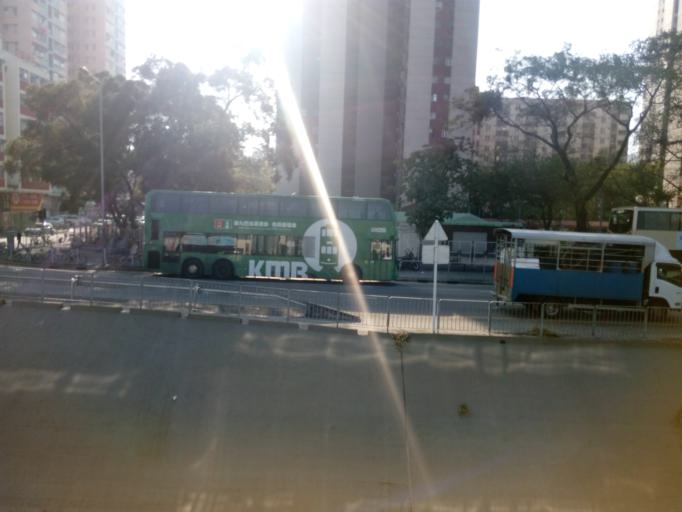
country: HK
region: Yuen Long
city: Yuen Long Kau Hui
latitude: 22.4466
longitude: 114.0205
